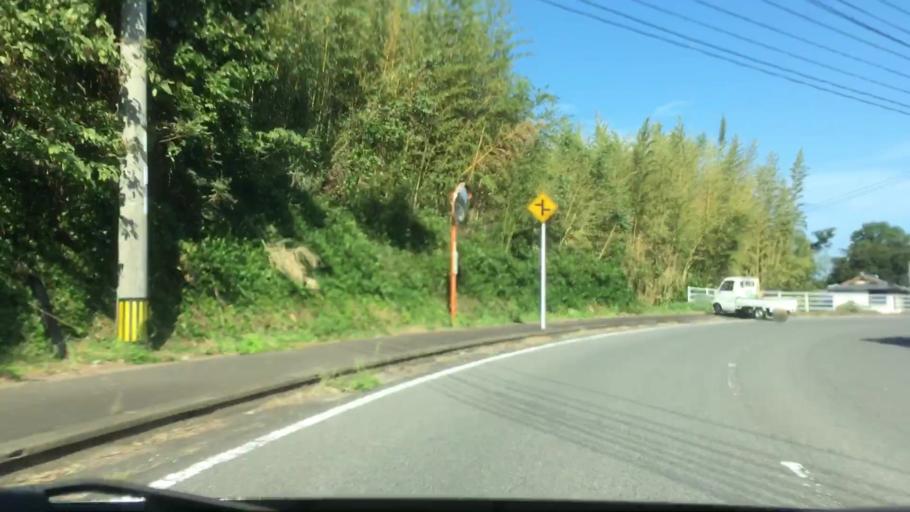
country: JP
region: Nagasaki
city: Sasebo
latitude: 33.0120
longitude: 129.6543
